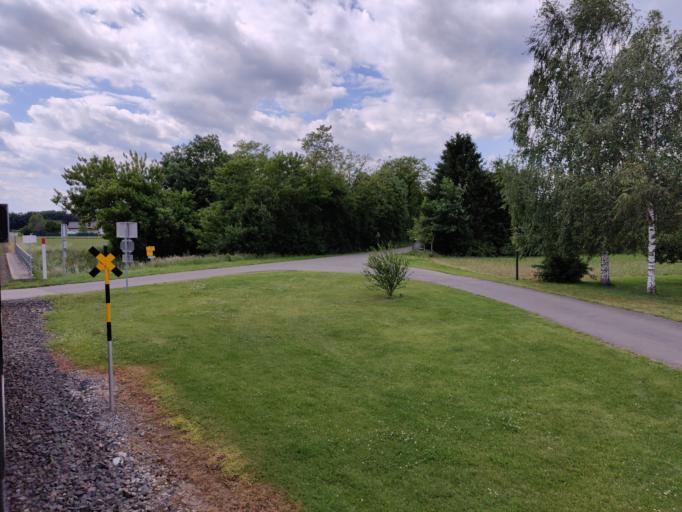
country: SI
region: Sentilj
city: Selnica ob Muri
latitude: 46.7146
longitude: 15.7135
